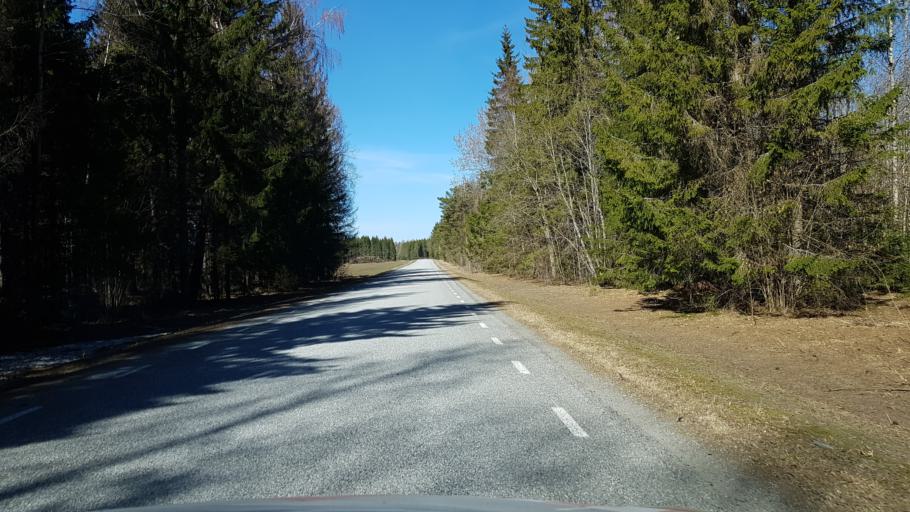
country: EE
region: Laeaene-Virumaa
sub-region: Vinni vald
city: Vinni
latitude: 59.1698
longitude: 26.5078
